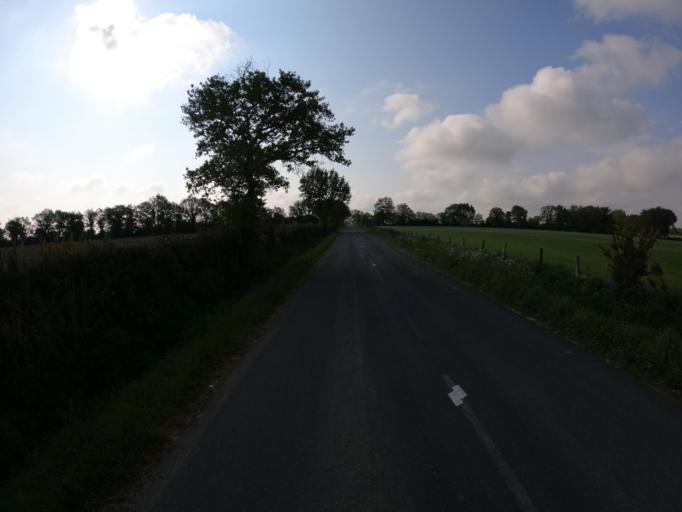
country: FR
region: Pays de la Loire
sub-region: Departement de Maine-et-Loire
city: La Romagne
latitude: 47.0681
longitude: -1.0457
